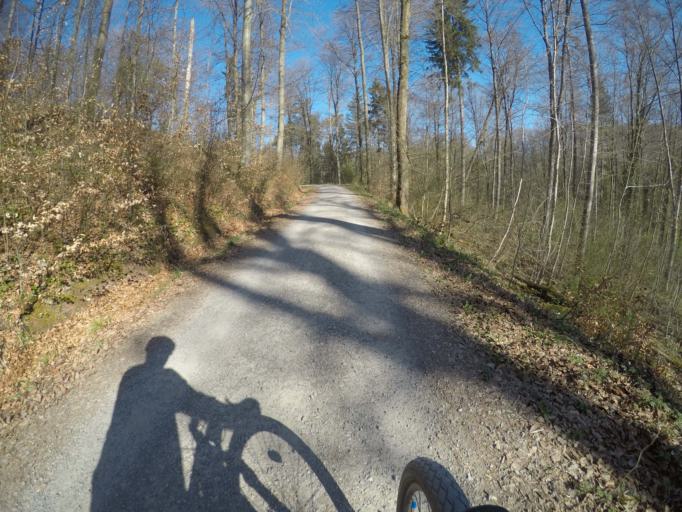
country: DE
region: Baden-Wuerttemberg
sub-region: Tuebingen Region
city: Dettenhausen
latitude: 48.6052
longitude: 9.1090
